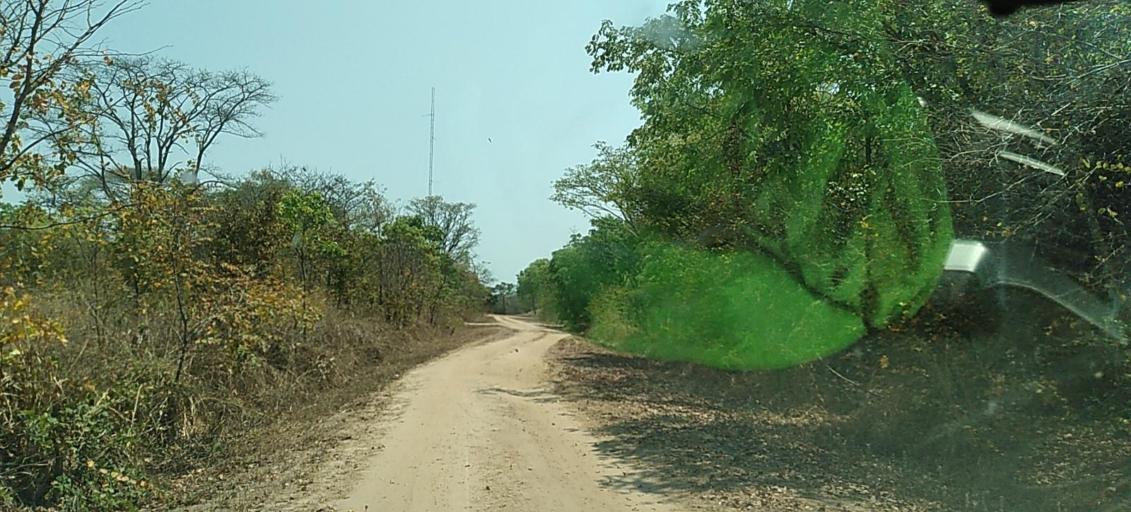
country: ZM
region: North-Western
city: Kalengwa
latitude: -13.1040
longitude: 24.6916
